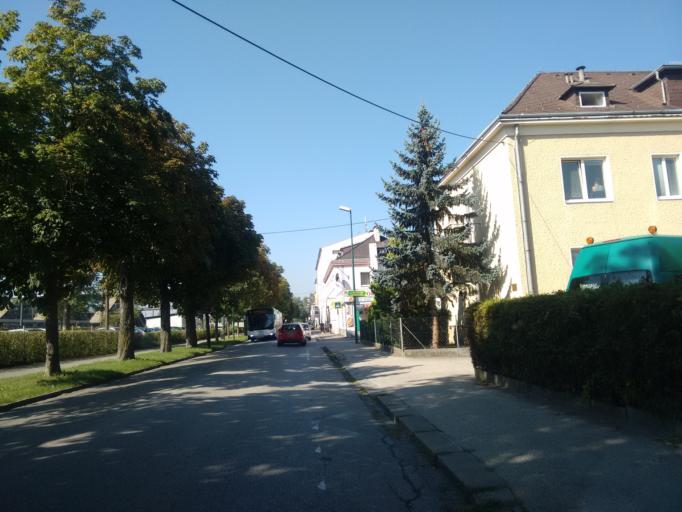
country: AT
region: Upper Austria
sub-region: Wels Stadt
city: Wels
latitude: 48.1674
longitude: 14.0284
